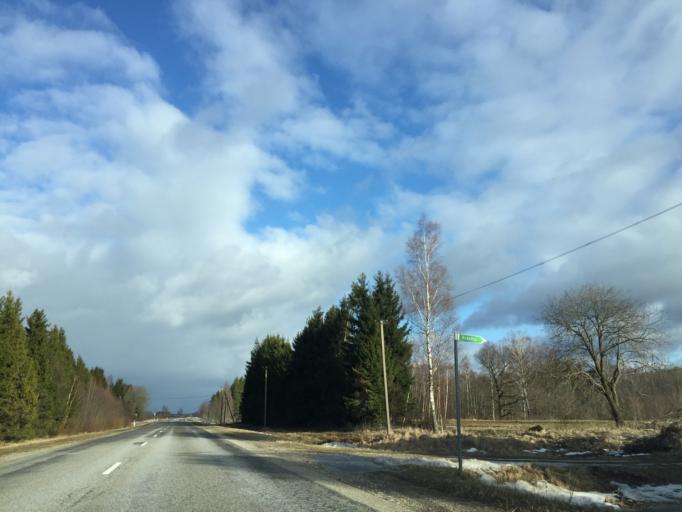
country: LV
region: Aloja
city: Staicele
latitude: 57.8703
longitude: 24.5705
